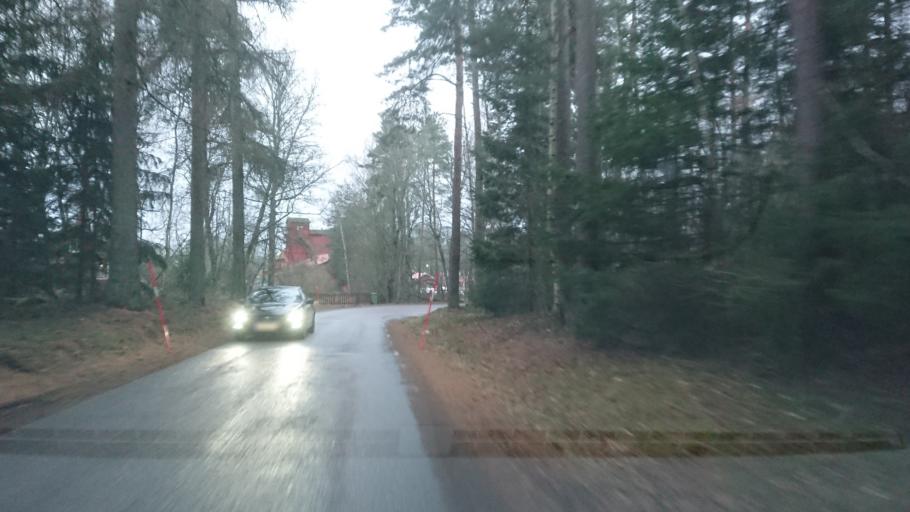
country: SE
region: Uppsala
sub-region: Osthammars Kommun
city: Bjorklinge
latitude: 60.0175
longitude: 17.5825
